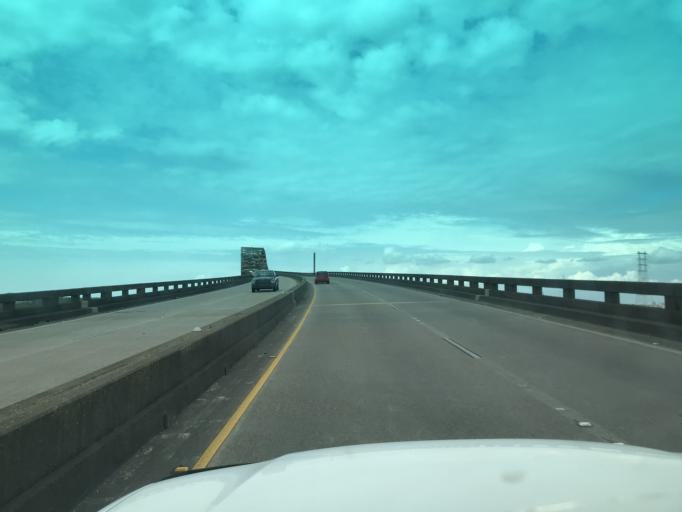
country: US
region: Louisiana
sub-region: Saint Bernard Parish
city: Chalmette
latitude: 29.9997
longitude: -89.9386
